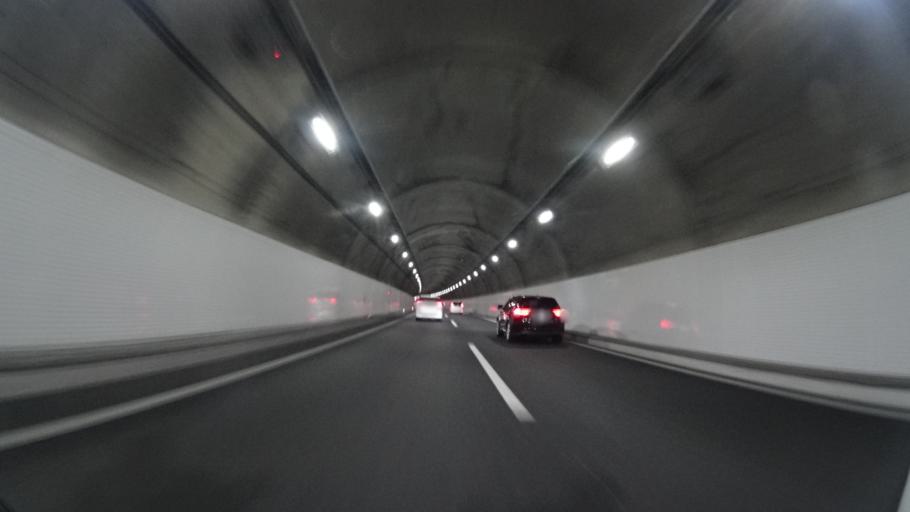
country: JP
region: Ehime
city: Saijo
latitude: 33.9070
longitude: 133.2165
